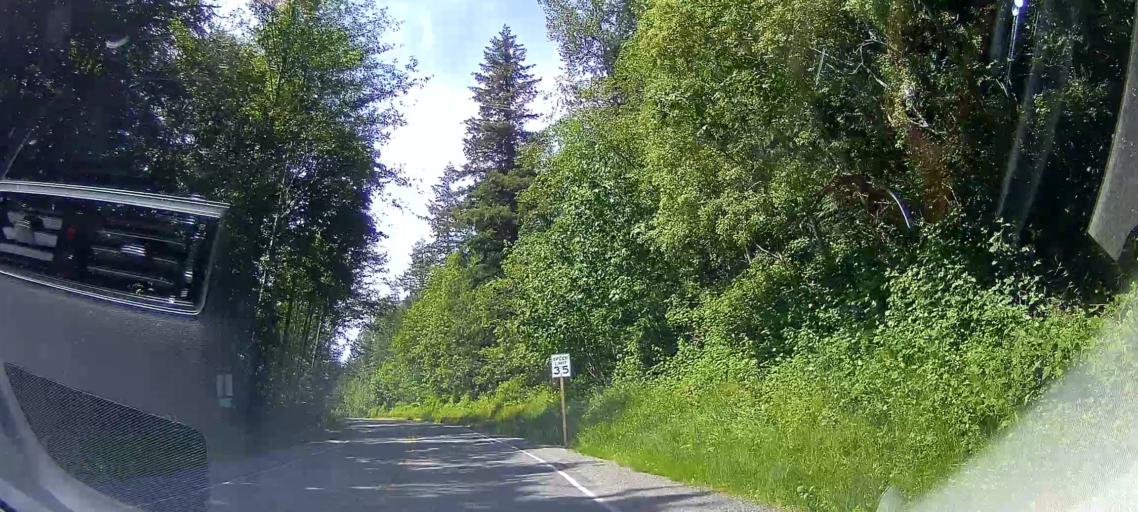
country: US
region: Washington
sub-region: Skagit County
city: Mount Vernon
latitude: 48.3971
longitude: -122.2924
